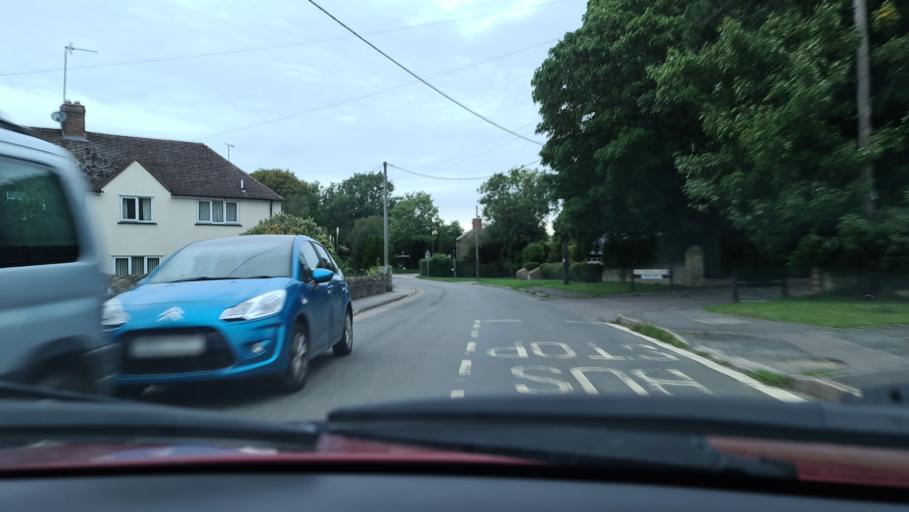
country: GB
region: England
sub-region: Oxfordshire
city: Somerton
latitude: 51.9607
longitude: -1.2330
